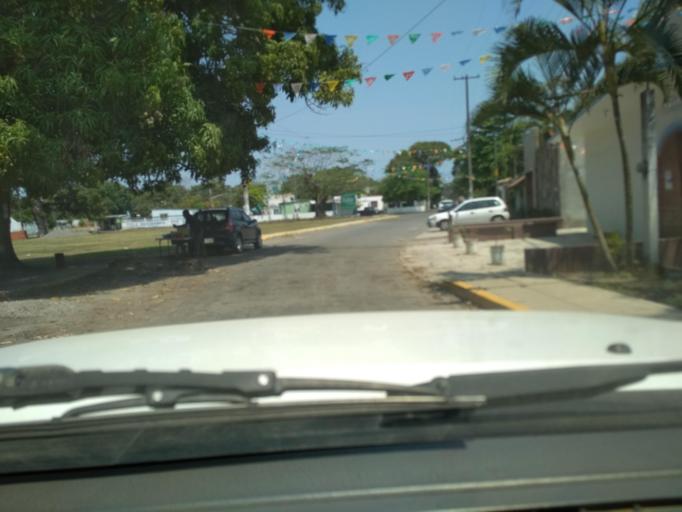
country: MX
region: Veracruz
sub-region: Medellin
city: Fraccionamiento Arboledas San Ramon
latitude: 19.0929
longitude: -96.1422
